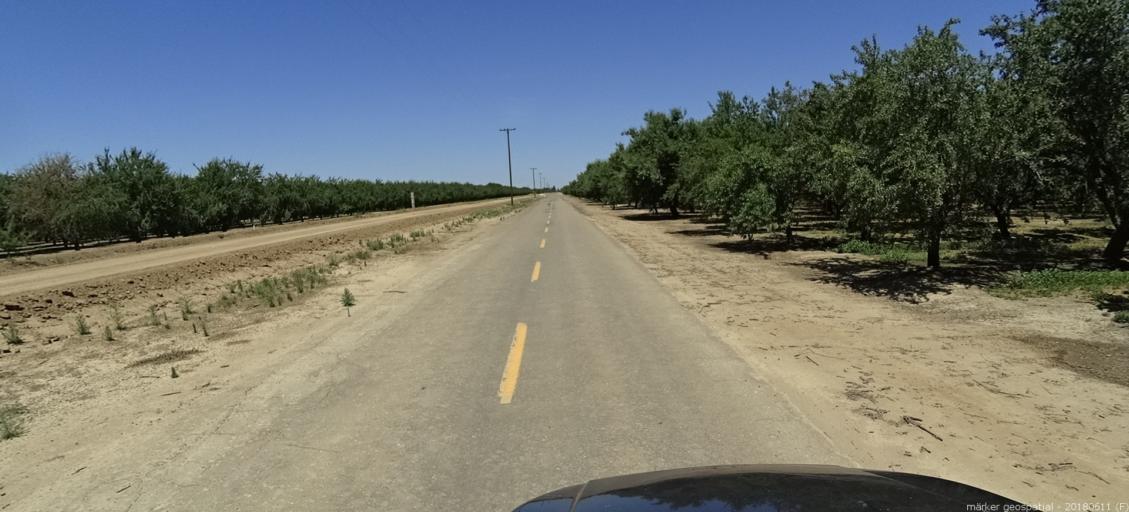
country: US
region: California
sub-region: Madera County
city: Fairmead
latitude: 37.0410
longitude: -120.1932
